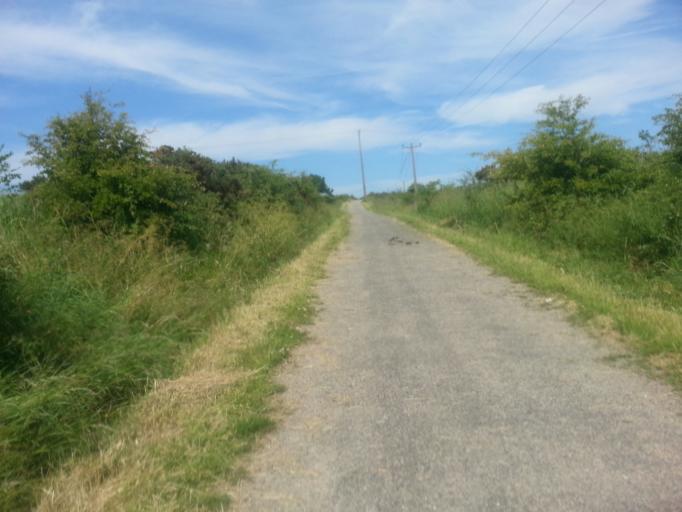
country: GB
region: England
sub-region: County Durham
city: Crook
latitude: 54.7297
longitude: -1.7396
